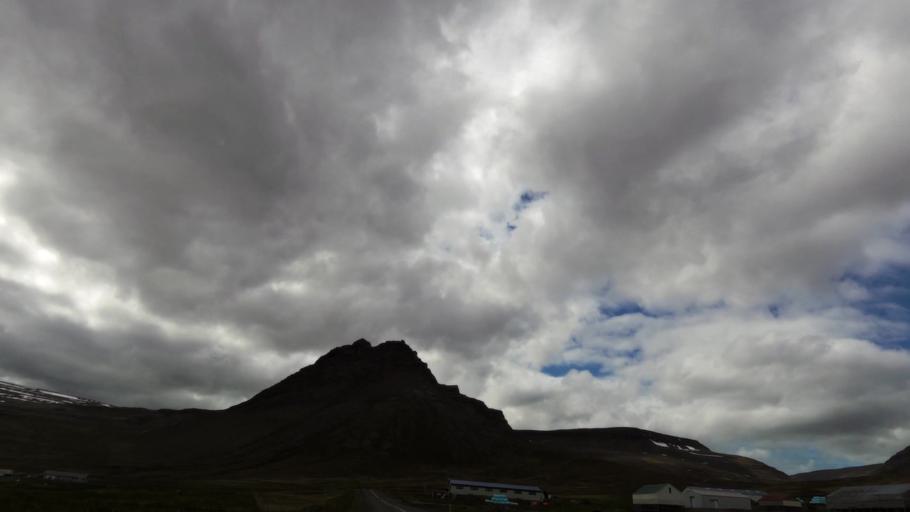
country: IS
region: Westfjords
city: Isafjoerdur
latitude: 66.1586
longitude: -23.2815
